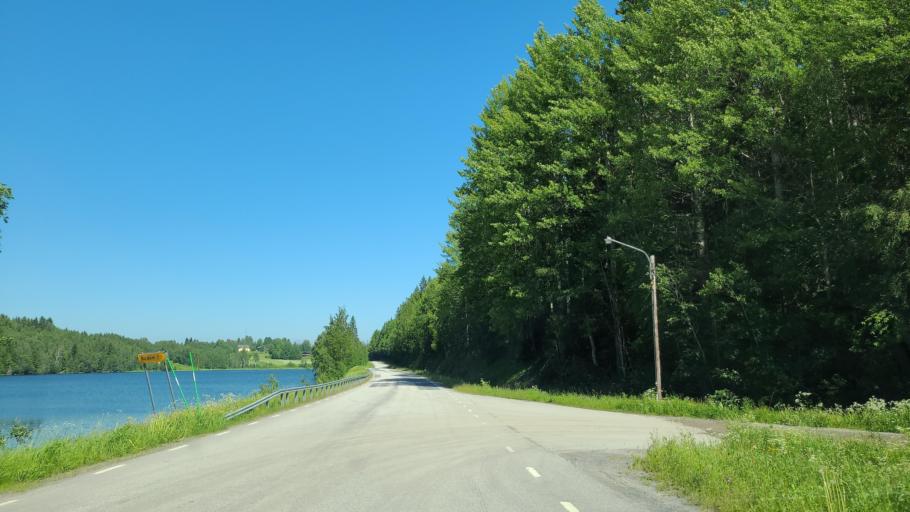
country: SE
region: Vaesternorrland
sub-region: OErnskoeldsviks Kommun
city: Husum
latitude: 63.3792
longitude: 19.1998
